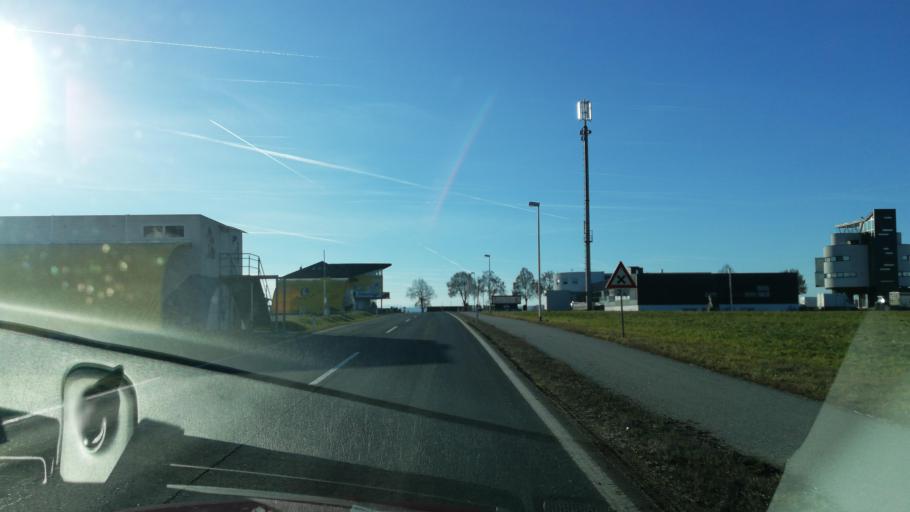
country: DE
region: Bavaria
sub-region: Upper Bavaria
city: Fridolfing
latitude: 48.0424
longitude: 12.8400
